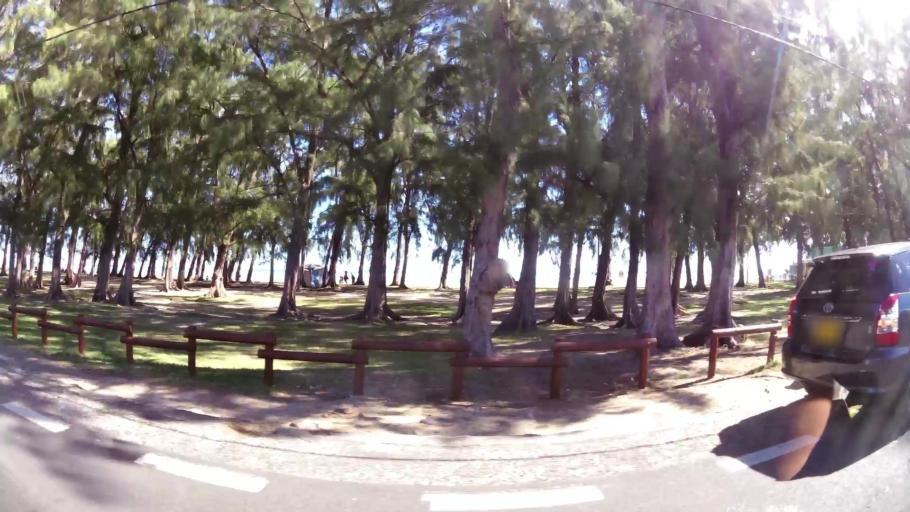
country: MU
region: Black River
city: Flic en Flac
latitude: -20.2820
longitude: 57.3655
